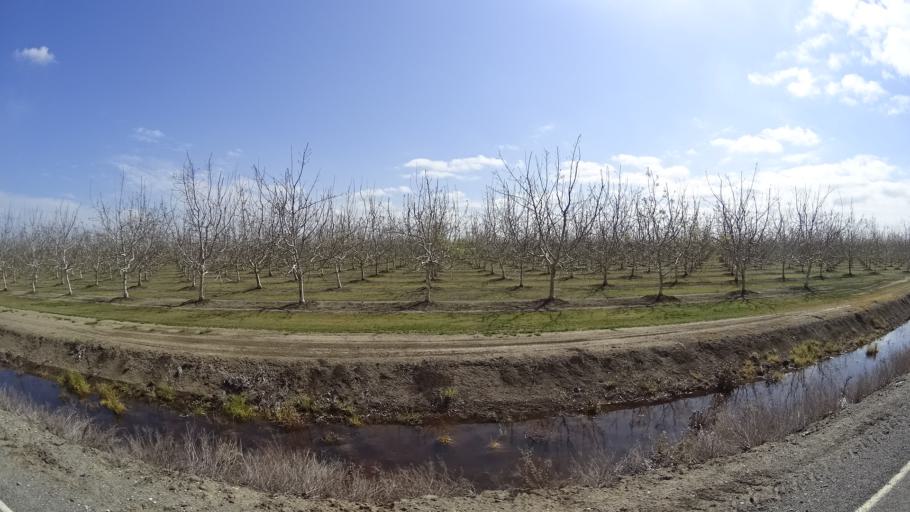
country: US
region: California
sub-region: Butte County
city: Biggs
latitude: 39.4462
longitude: -121.9302
